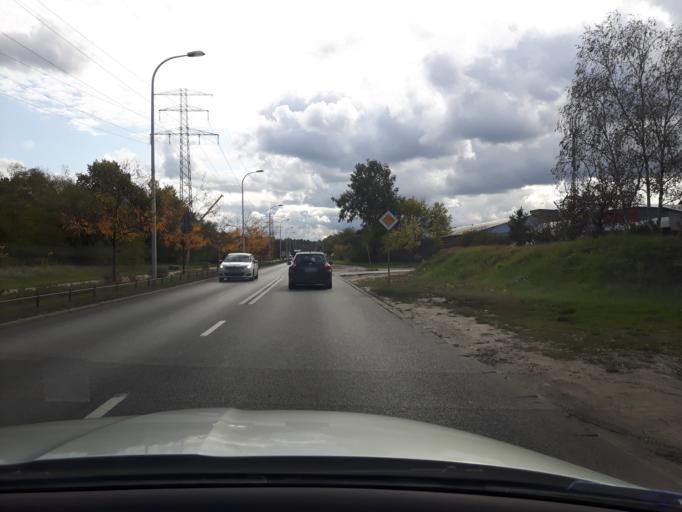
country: PL
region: Masovian Voivodeship
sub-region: Warszawa
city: Rembertow
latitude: 52.2397
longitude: 21.1409
